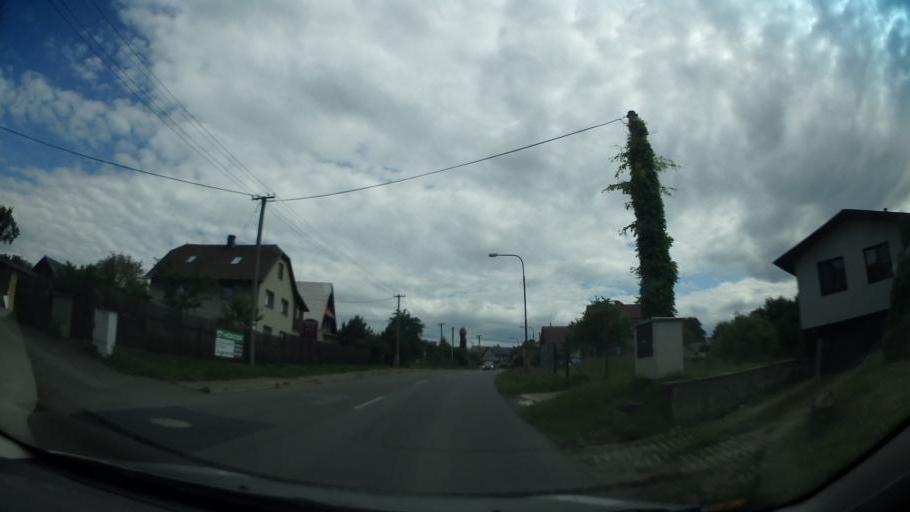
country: CZ
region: Pardubicky
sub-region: Okres Svitavy
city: Moravska Trebova
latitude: 49.7918
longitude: 16.6725
